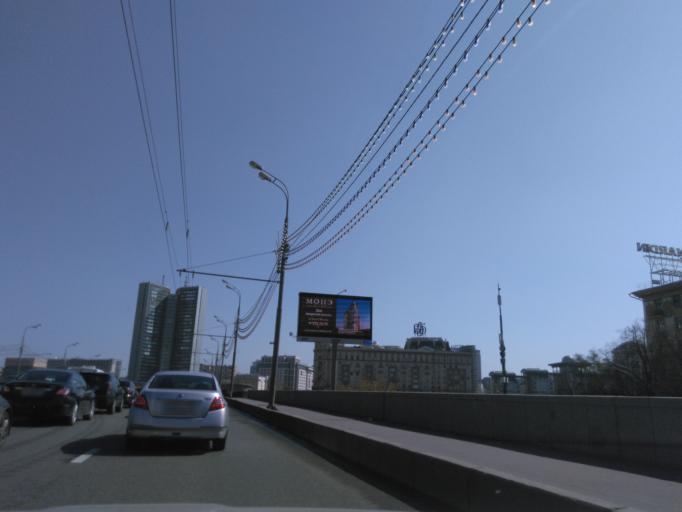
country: RU
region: Moskovskaya
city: Dorogomilovo
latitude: 55.7511
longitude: 37.5693
